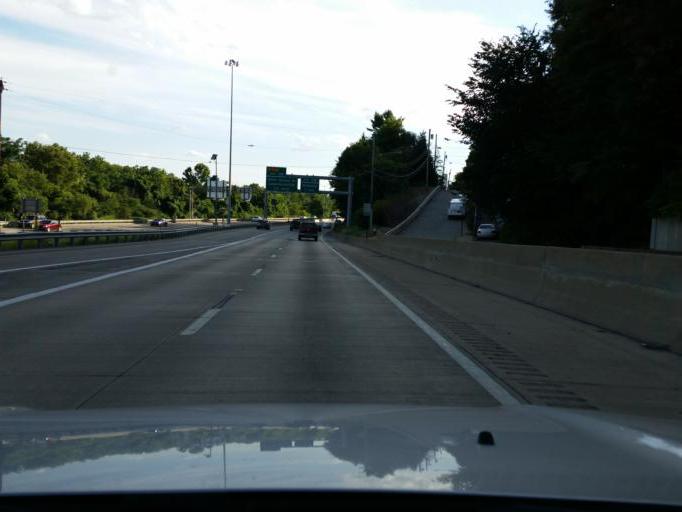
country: US
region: Pennsylvania
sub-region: Allegheny County
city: Etna
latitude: 40.4916
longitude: -79.9511
